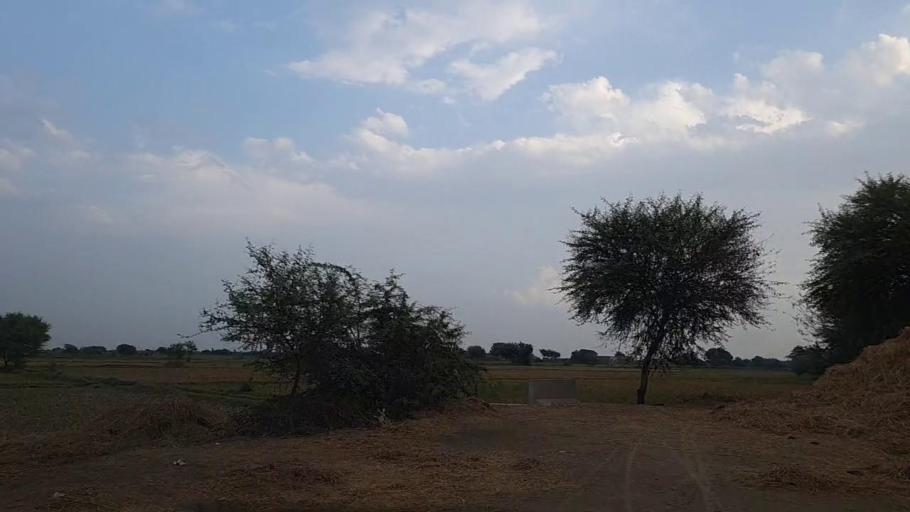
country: PK
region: Sindh
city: Daro Mehar
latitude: 24.7701
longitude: 68.1422
